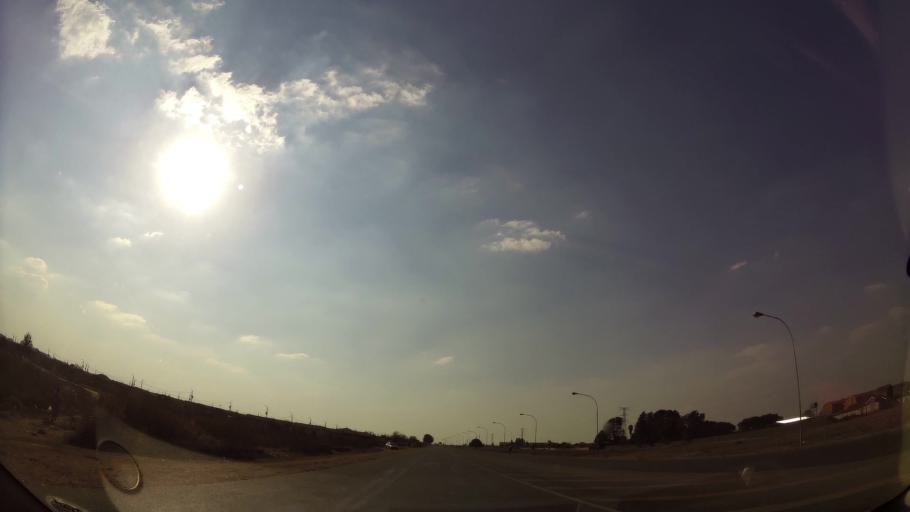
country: ZA
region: Gauteng
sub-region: Ekurhuleni Metropolitan Municipality
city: Benoni
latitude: -26.1571
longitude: 28.3969
